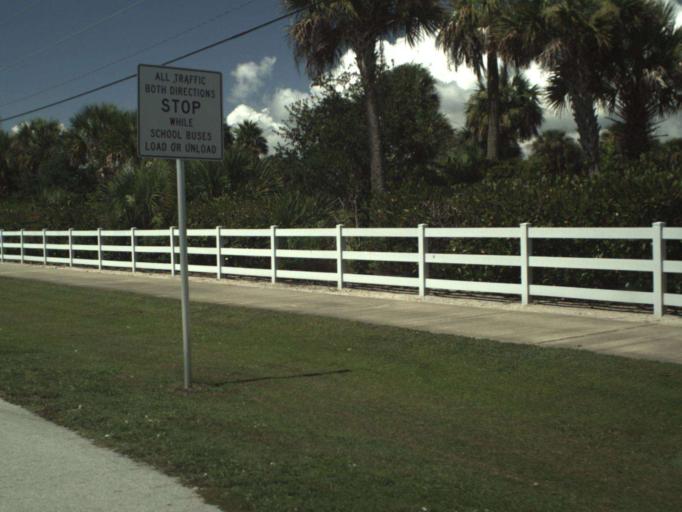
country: US
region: Florida
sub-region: Indian River County
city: South Beach
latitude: 27.5909
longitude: -80.3333
